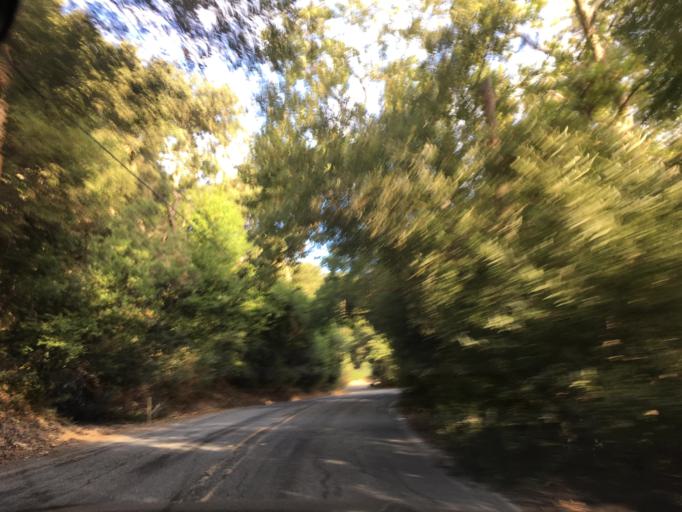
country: US
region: California
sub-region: Santa Clara County
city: Cambrian Park
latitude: 37.2194
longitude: -121.9224
